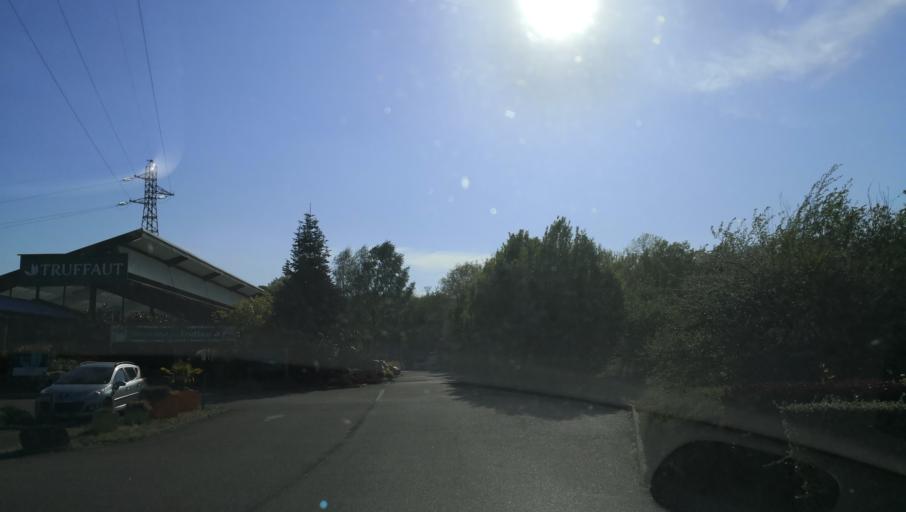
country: FR
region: Limousin
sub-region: Departement de la Haute-Vienne
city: Couzeix
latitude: 45.8666
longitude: 1.2679
